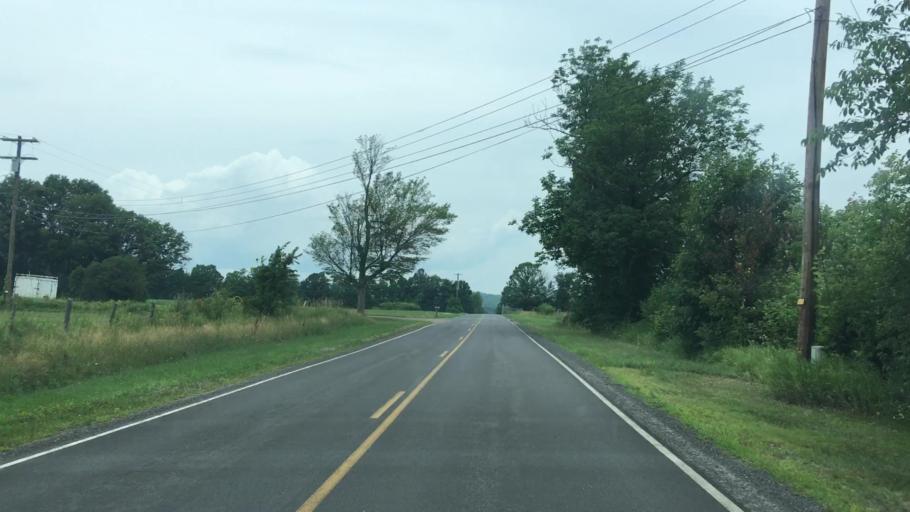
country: US
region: New York
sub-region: Clinton County
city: Peru
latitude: 44.5980
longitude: -73.6276
